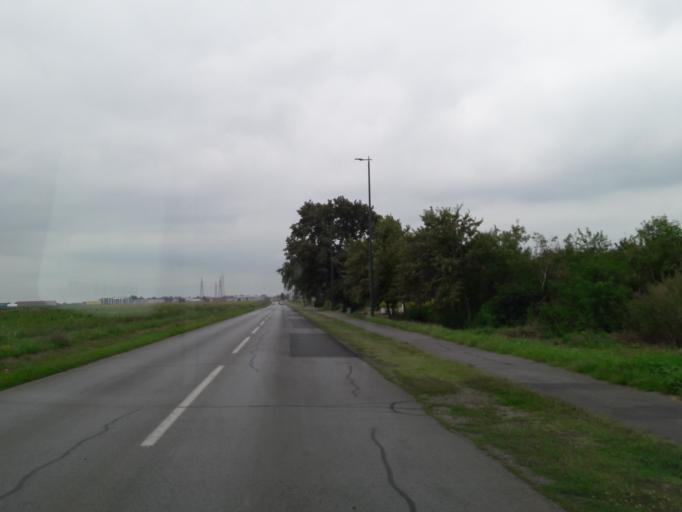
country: HR
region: Osjecko-Baranjska
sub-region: Grad Osijek
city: Osijek
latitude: 45.5287
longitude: 18.7213
